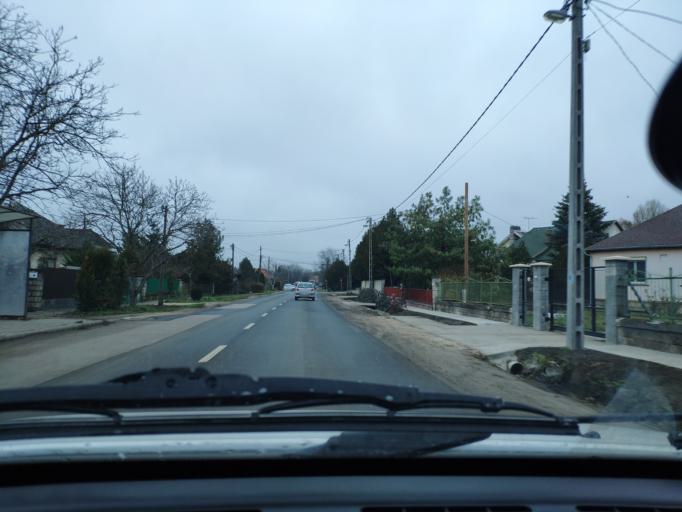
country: HU
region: Pest
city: Soskut
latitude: 47.4003
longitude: 18.8377
